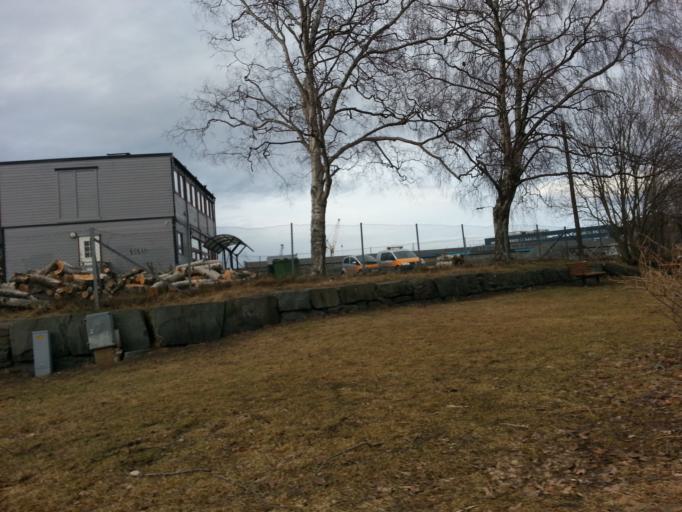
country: NO
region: Sor-Trondelag
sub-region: Trondheim
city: Trondheim
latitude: 63.4370
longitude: 10.4185
